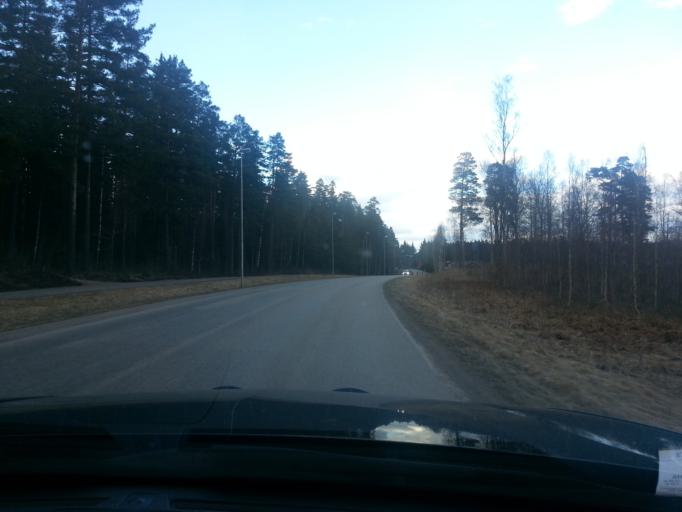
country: SE
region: Joenkoeping
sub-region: Vetlanda Kommun
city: Vetlanda
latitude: 57.4089
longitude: 15.0547
